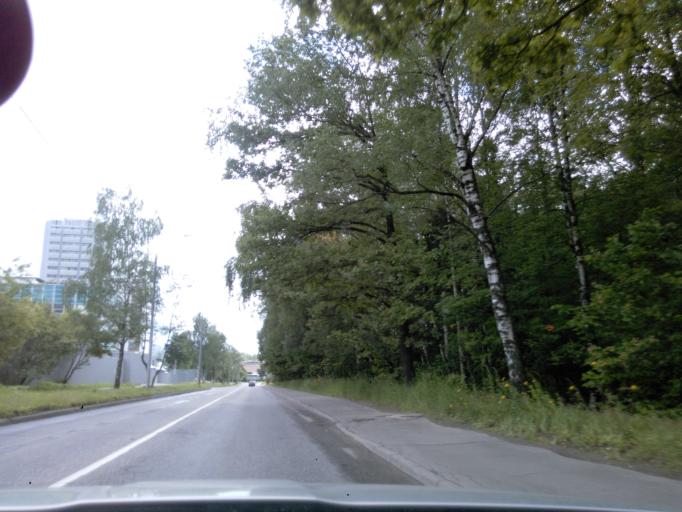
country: RU
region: Moskovskaya
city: Mendeleyevo
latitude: 56.0161
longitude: 37.1931
